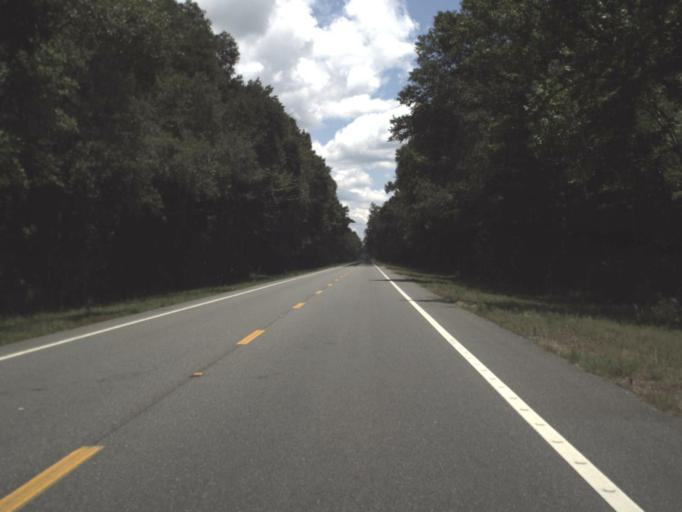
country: US
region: Florida
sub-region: Leon County
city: Woodville
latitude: 30.1436
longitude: -83.9623
